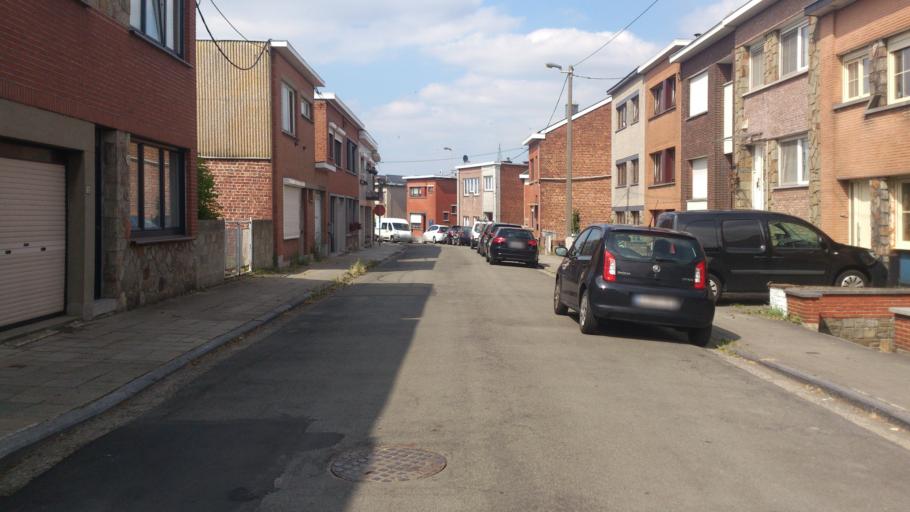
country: BE
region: Wallonia
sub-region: Province de Liege
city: Beyne-Heusay
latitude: 50.6258
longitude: 5.6548
